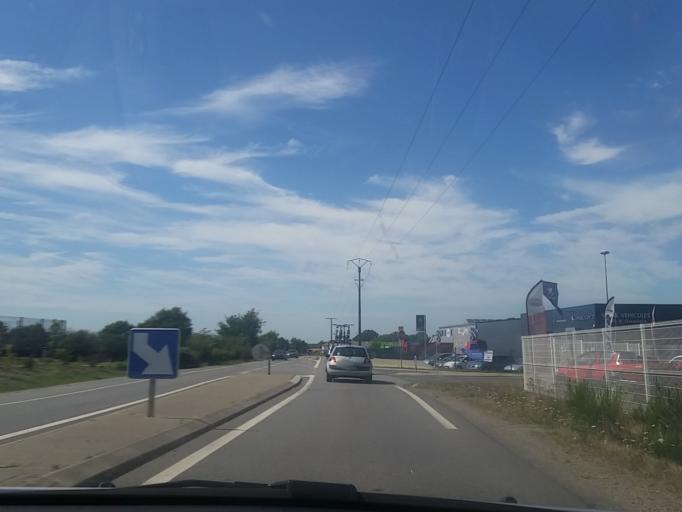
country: FR
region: Pays de la Loire
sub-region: Departement de la Loire-Atlantique
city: Saint-Pere-en-Retz
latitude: 47.1964
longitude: -2.0300
